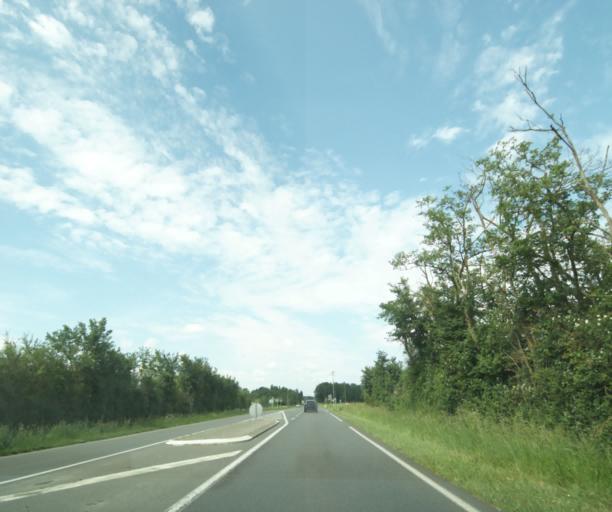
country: FR
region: Pays de la Loire
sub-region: Departement de Maine-et-Loire
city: Montreuil-Bellay
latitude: 47.1766
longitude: -0.1354
